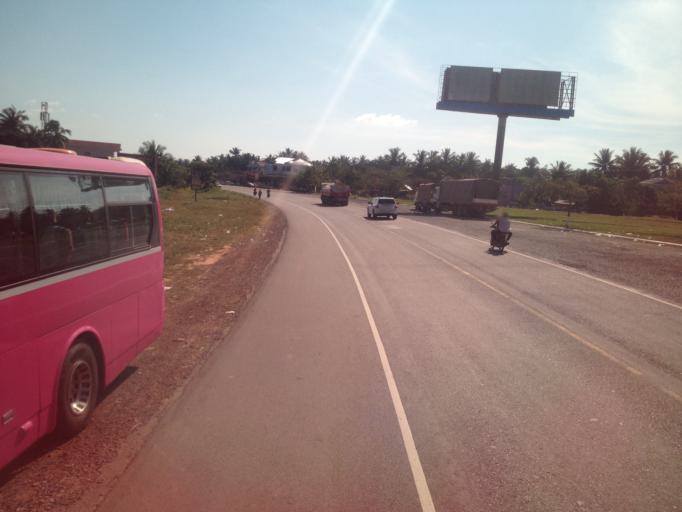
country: KH
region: Preah Sihanouk
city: Sihanoukville
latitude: 10.5858
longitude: 103.6442
